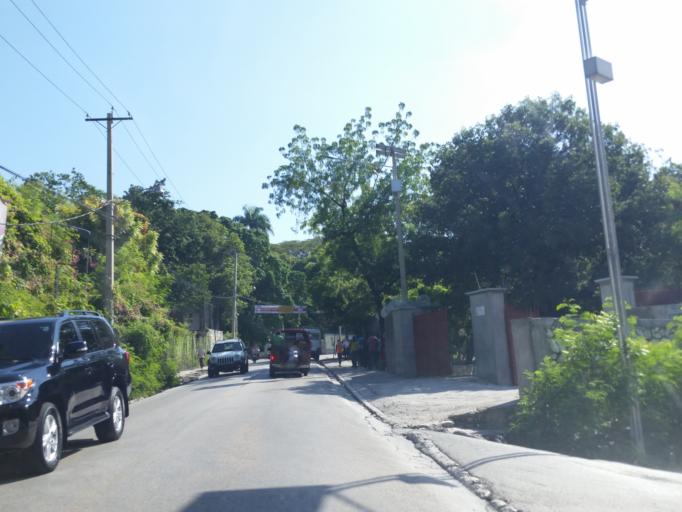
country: HT
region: Ouest
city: Delmas 73
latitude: 18.5368
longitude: -72.3126
